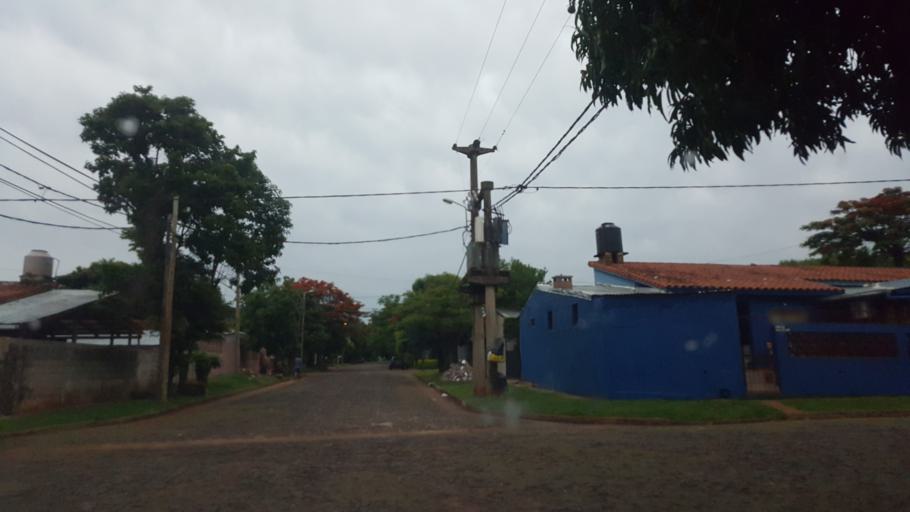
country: AR
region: Misiones
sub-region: Departamento de Capital
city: Posadas
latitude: -27.3764
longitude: -55.9235
